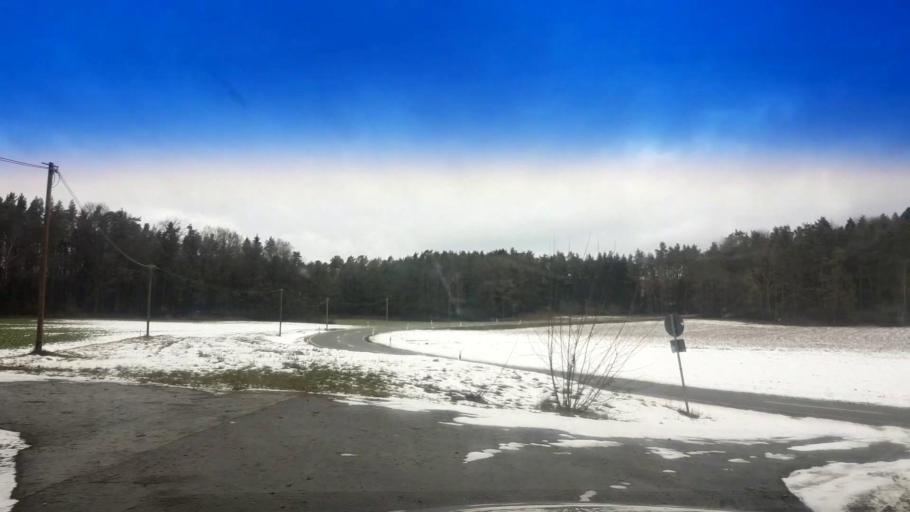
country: DE
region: Bavaria
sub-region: Upper Franconia
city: Wattendorf
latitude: 49.9959
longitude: 11.1307
